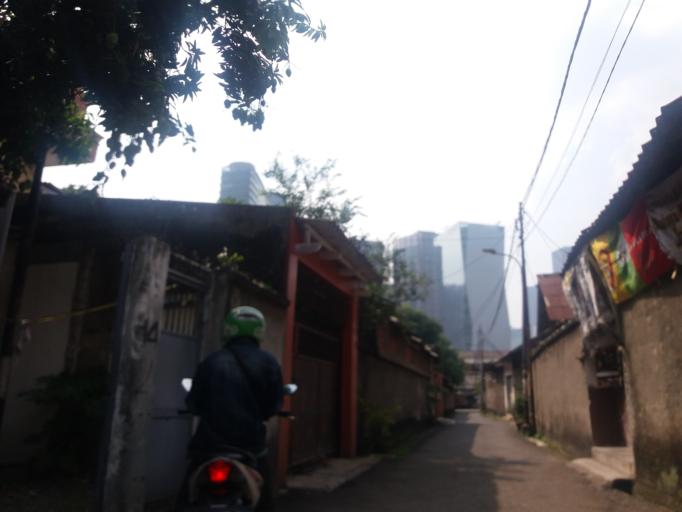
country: ID
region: Jakarta Raya
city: Jakarta
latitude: -6.2223
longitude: 106.8179
